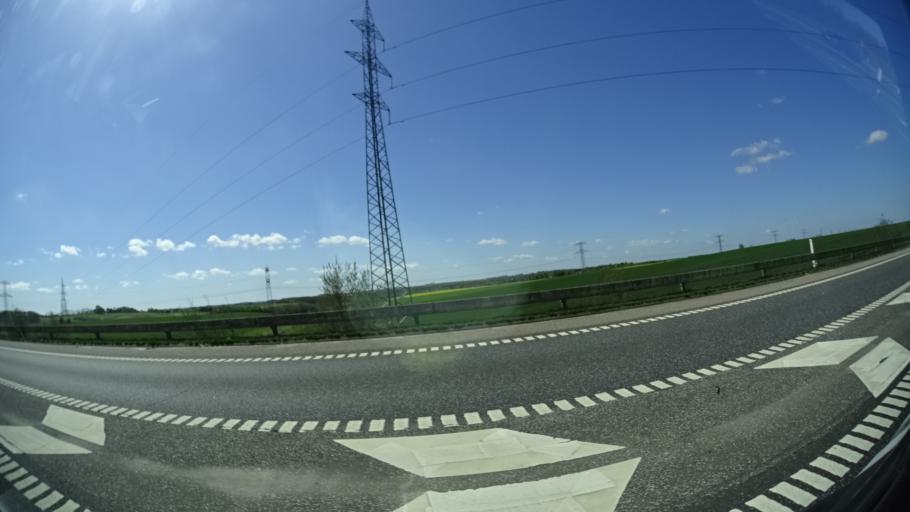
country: DK
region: Central Jutland
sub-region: Arhus Kommune
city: Trige
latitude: 56.3092
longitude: 10.1197
